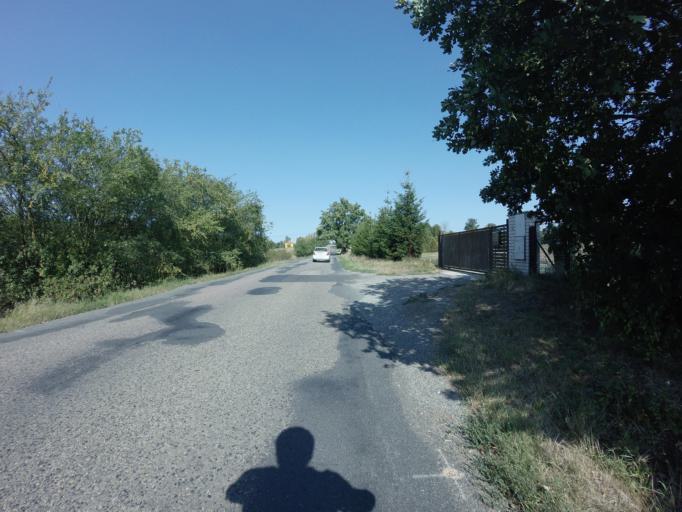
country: CZ
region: Central Bohemia
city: Tynec nad Sazavou
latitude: 49.8437
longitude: 14.5595
